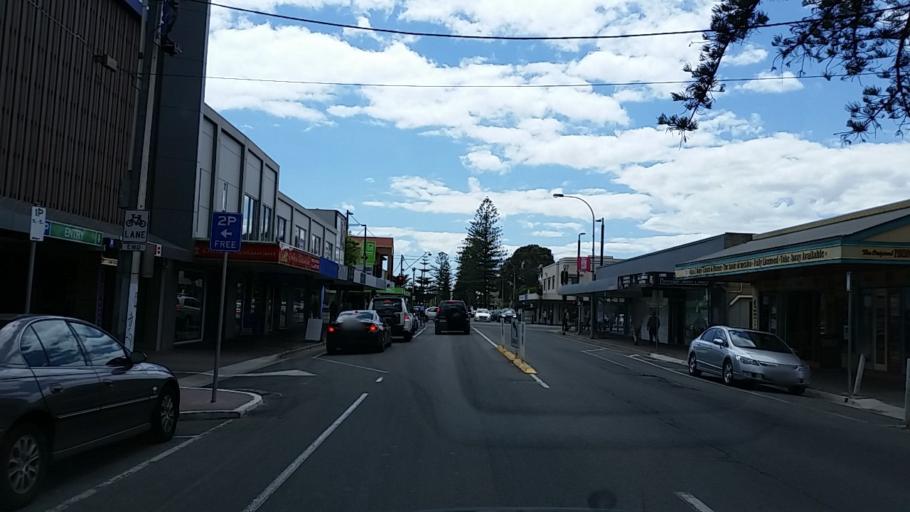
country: AU
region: South Australia
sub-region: Adelaide
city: Glenelg
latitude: -34.9808
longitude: 138.5178
